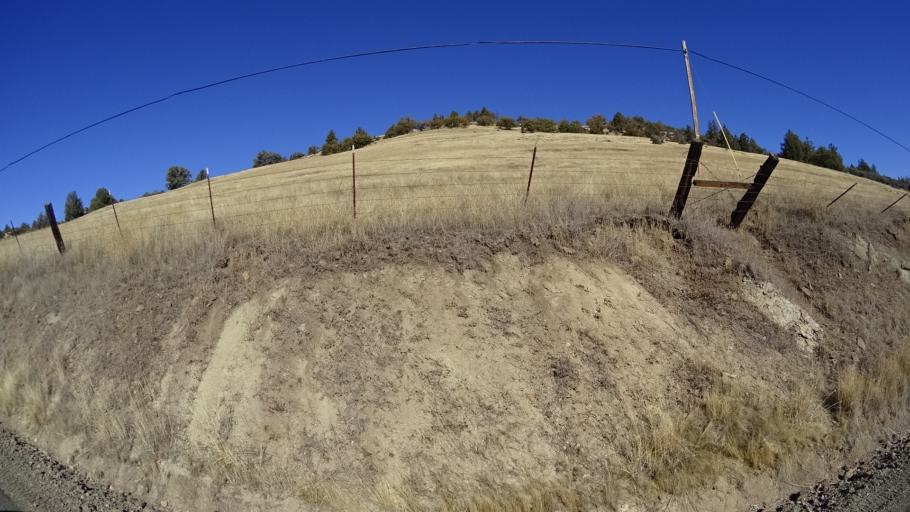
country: US
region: California
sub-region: Siskiyou County
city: Montague
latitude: 41.9616
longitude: -122.3139
